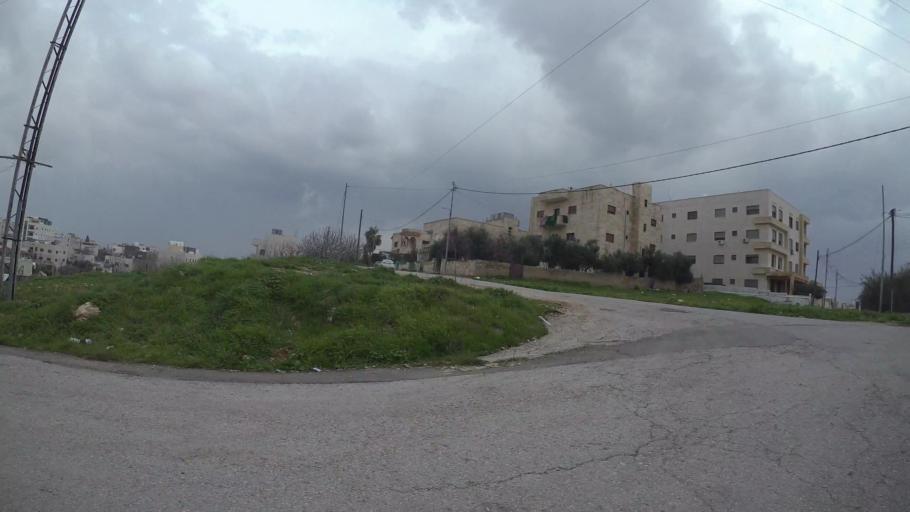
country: JO
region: Amman
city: Umm as Summaq
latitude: 31.8838
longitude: 35.8579
